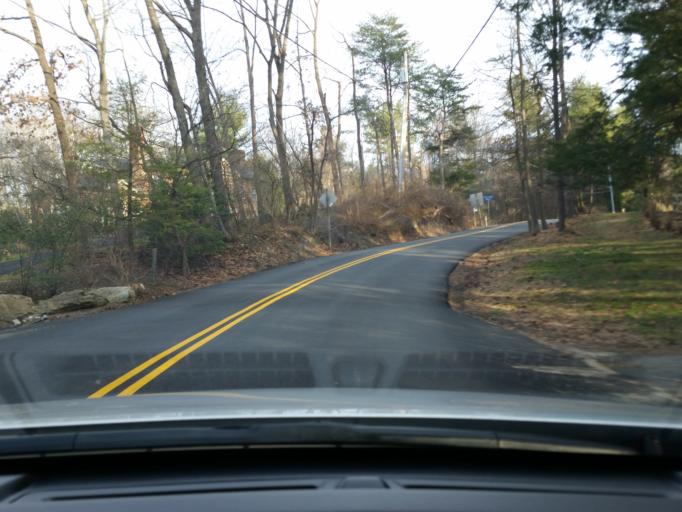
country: US
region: Virginia
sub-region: Fairfax County
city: Great Falls
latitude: 38.9700
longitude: -77.2673
